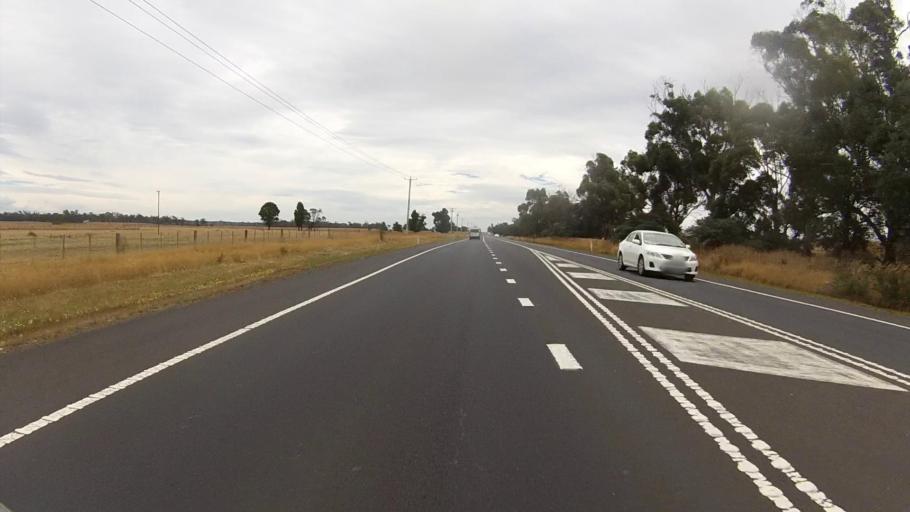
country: AU
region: Tasmania
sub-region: Northern Midlands
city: Evandale
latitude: -41.6872
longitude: 147.2784
